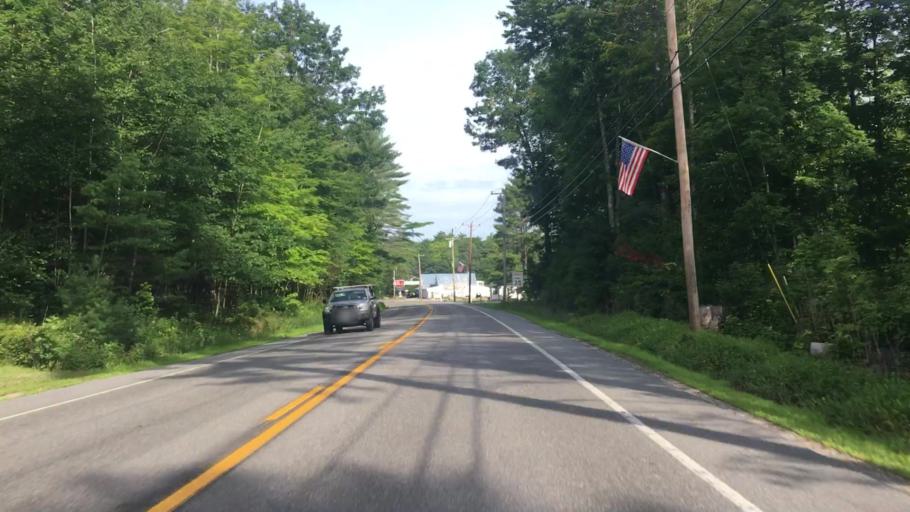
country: US
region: Maine
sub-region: York County
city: Cornish
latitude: 43.8021
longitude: -70.7899
